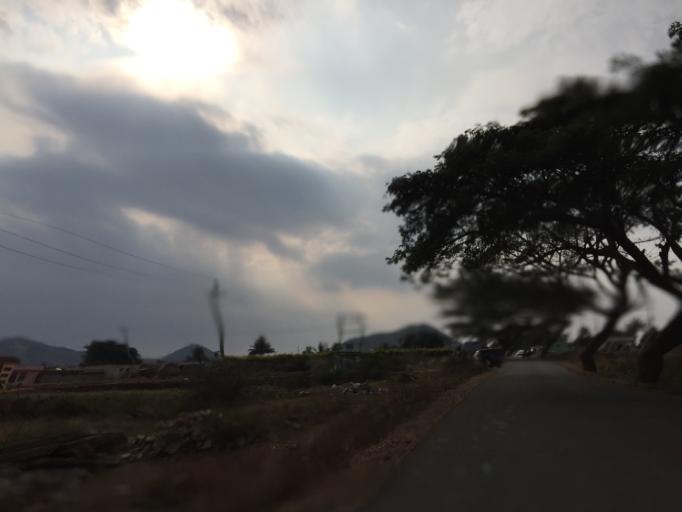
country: IN
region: Karnataka
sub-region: Chikkaballapur
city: Chik Ballapur
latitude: 13.5516
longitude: 77.7570
